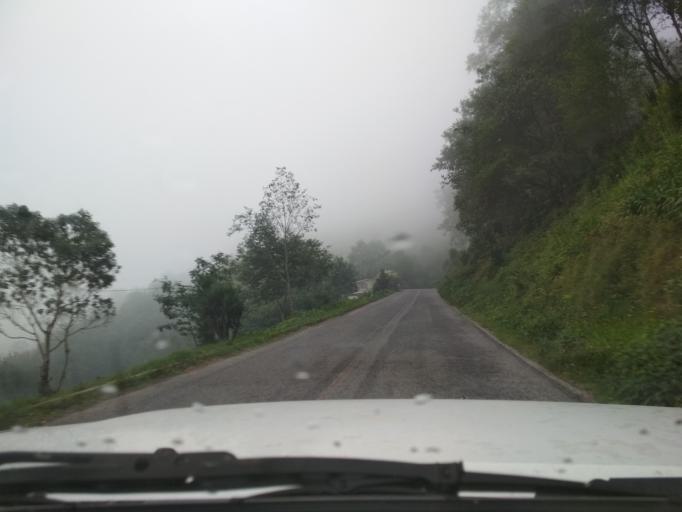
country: MX
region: Veracruz
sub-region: La Perla
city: Metlac Hernandez (Metlac Primero)
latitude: 18.9522
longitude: -97.1715
